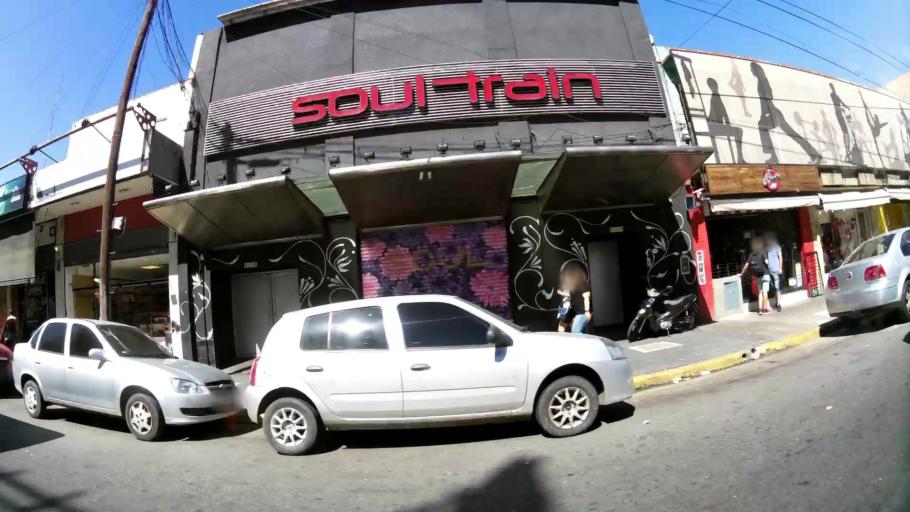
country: AR
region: Buenos Aires
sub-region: Partido de General San Martin
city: General San Martin
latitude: -34.5761
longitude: -58.5384
